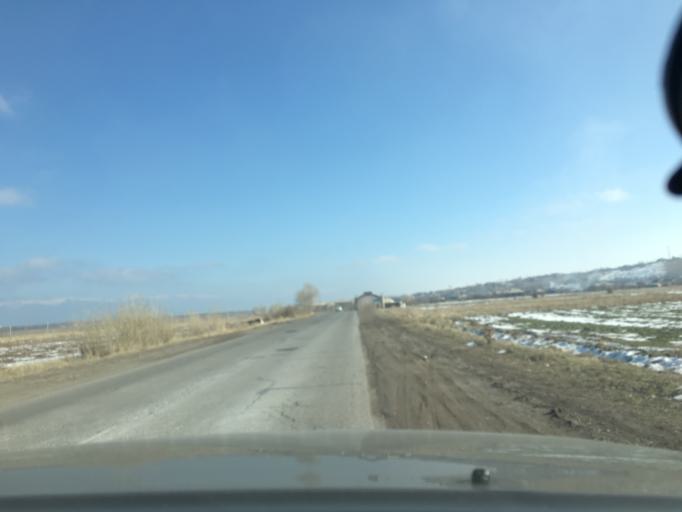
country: AM
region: Geghark'unik'i Marz
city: Tsovinar
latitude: 40.1563
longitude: 45.4445
